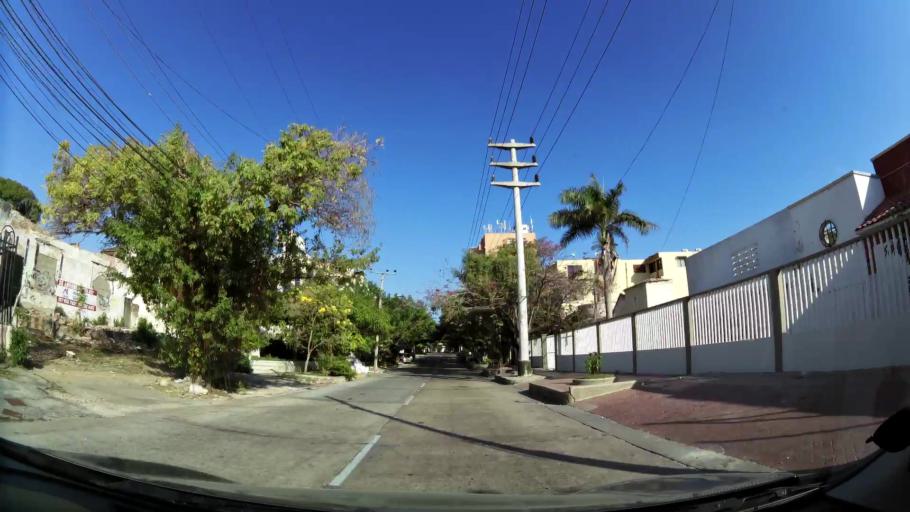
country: CO
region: Atlantico
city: Barranquilla
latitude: 11.0042
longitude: -74.7982
